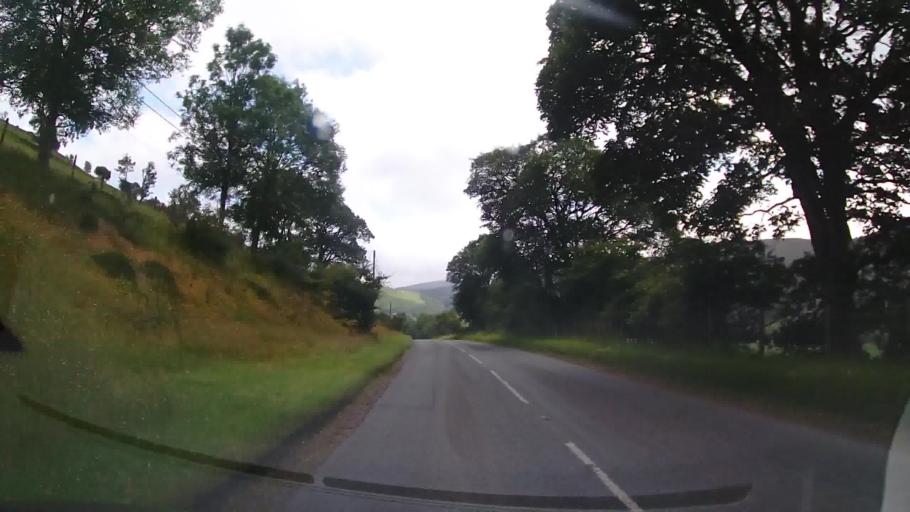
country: GB
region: Wales
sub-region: Sir Powys
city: Llangynog
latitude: 52.8417
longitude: -3.4225
